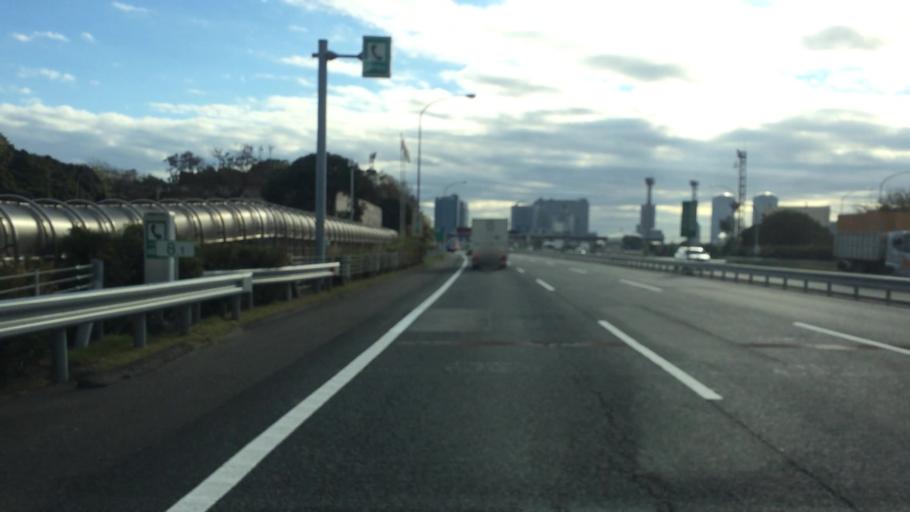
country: JP
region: Chiba
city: Funabashi
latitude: 35.6630
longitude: 140.0218
